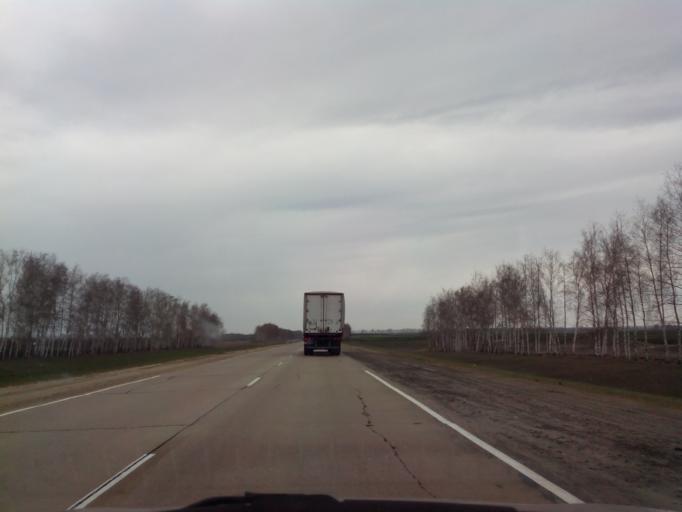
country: RU
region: Tambov
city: Pokrovo-Prigorodnoye
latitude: 52.6432
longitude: 41.3413
